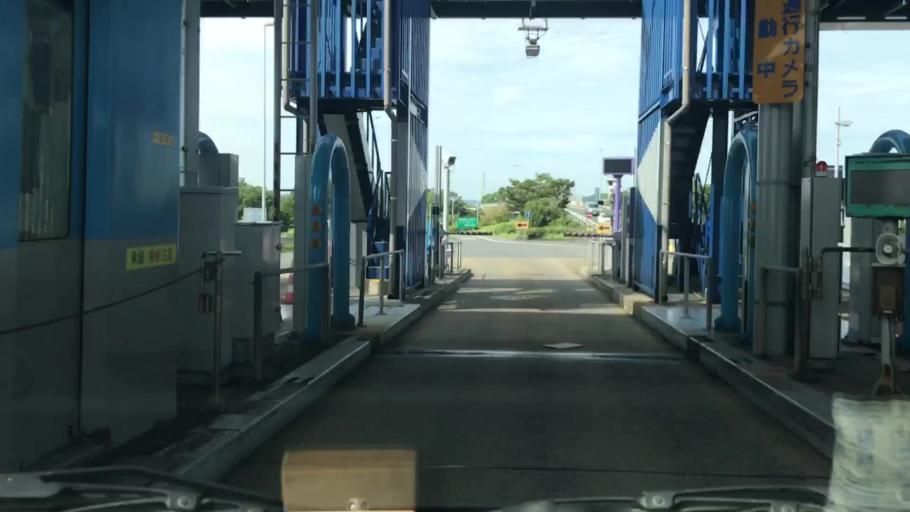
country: JP
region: Saga Prefecture
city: Saga-shi
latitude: 33.3197
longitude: 130.2768
